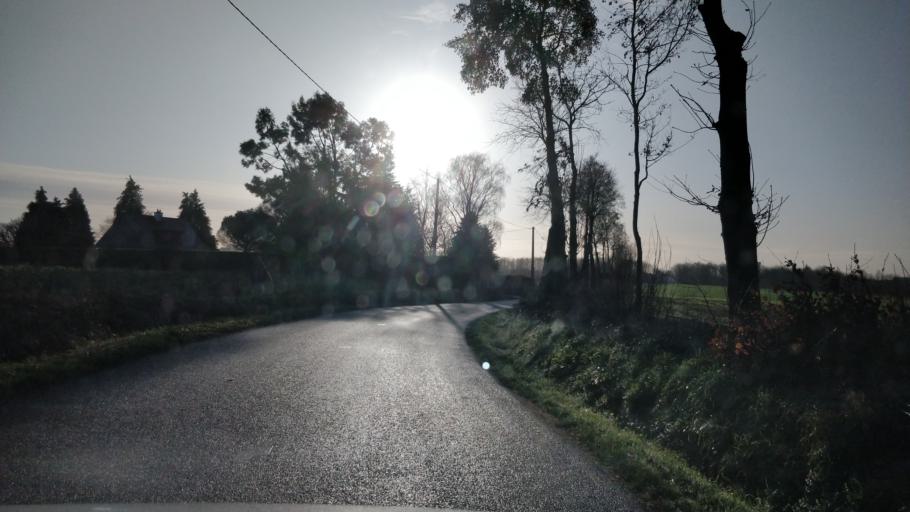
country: FR
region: Brittany
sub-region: Departement d'Ille-et-Vilaine
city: Chavagne
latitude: 48.0633
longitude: -1.7902
